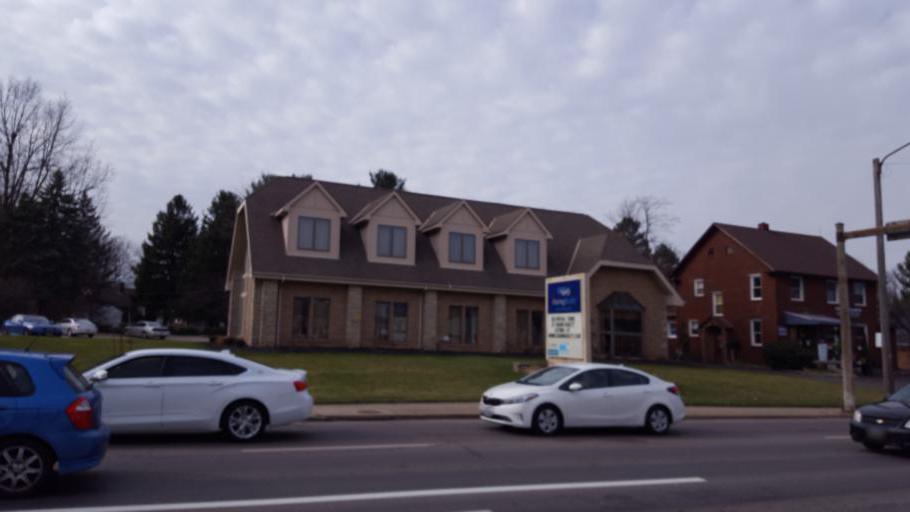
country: US
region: Ohio
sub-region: Richland County
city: Mansfield
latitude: 40.7264
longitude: -82.5397
